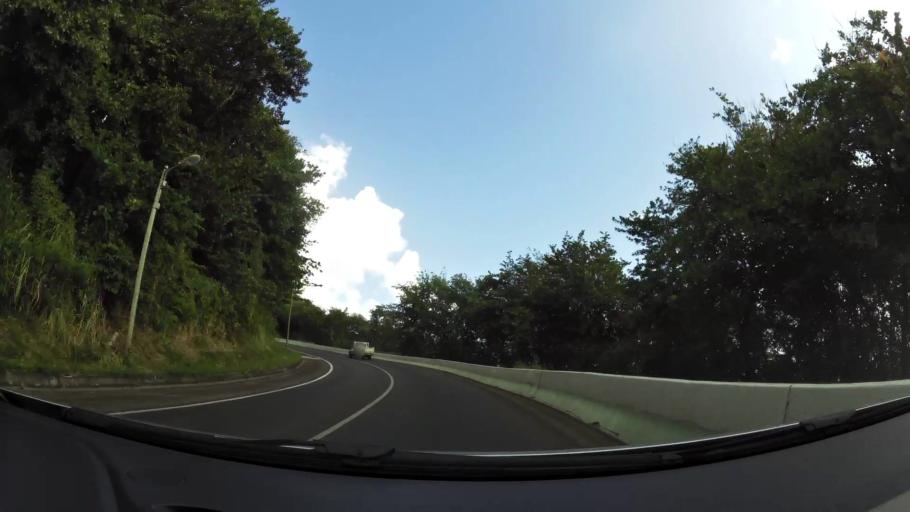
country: MQ
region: Martinique
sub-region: Martinique
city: Le Lorrain
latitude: 14.8262
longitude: -61.0315
